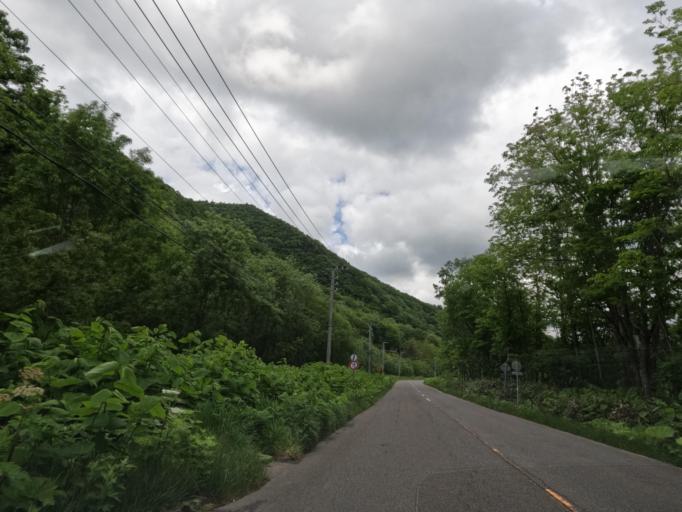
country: JP
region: Hokkaido
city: Takikawa
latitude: 43.5656
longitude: 141.7028
